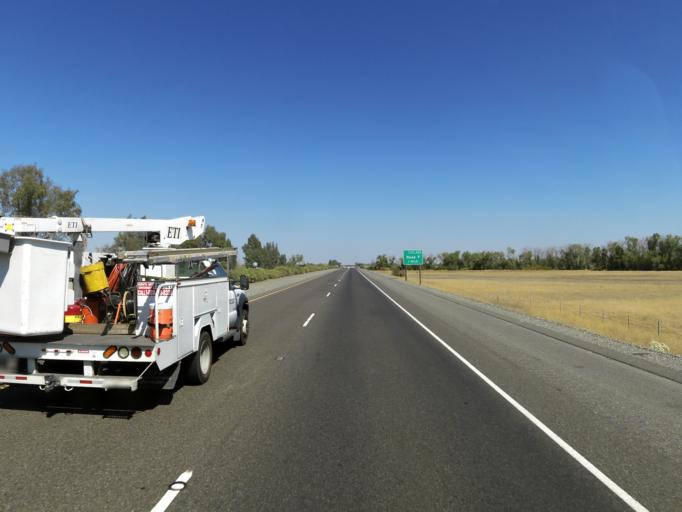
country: US
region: California
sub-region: Glenn County
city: Orland
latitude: 39.7658
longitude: -122.2050
